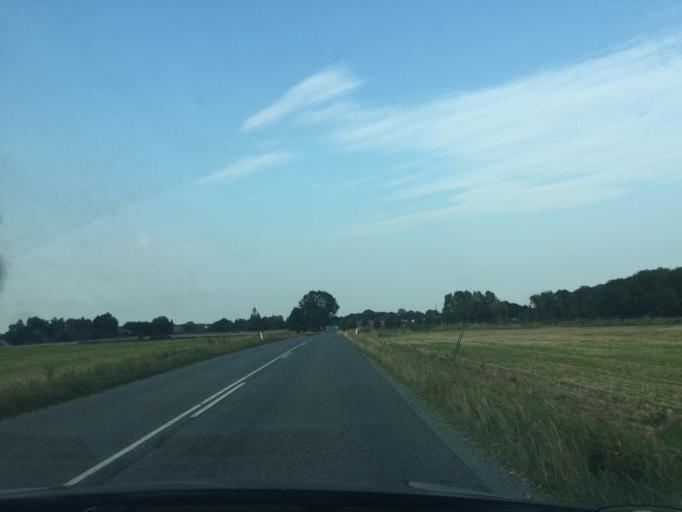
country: DK
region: South Denmark
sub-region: Kerteminde Kommune
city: Langeskov
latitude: 55.3019
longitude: 10.5772
